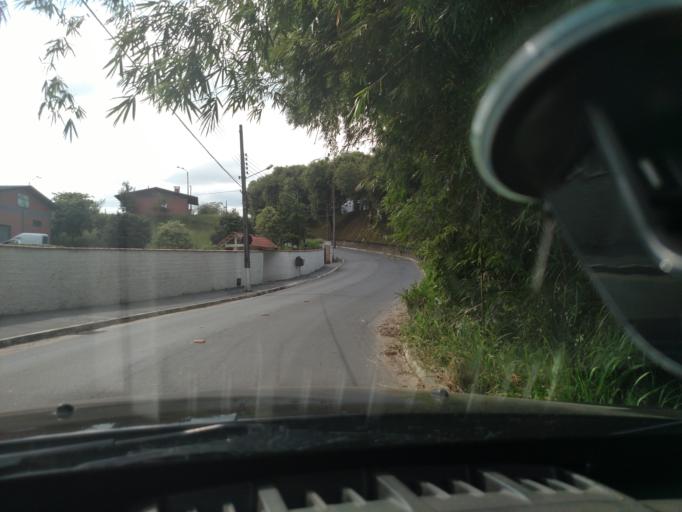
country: BR
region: Santa Catarina
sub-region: Indaial
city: Indaial
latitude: -26.8962
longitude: -49.2605
